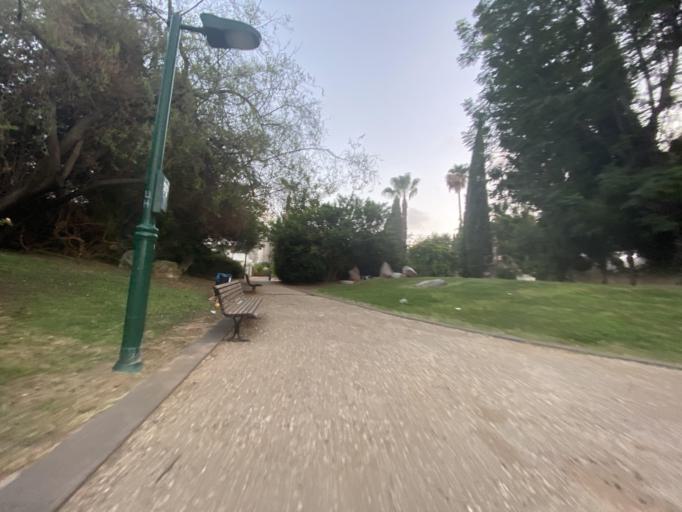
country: IL
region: Tel Aviv
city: Ramat HaSharon
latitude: 32.1462
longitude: 34.8417
